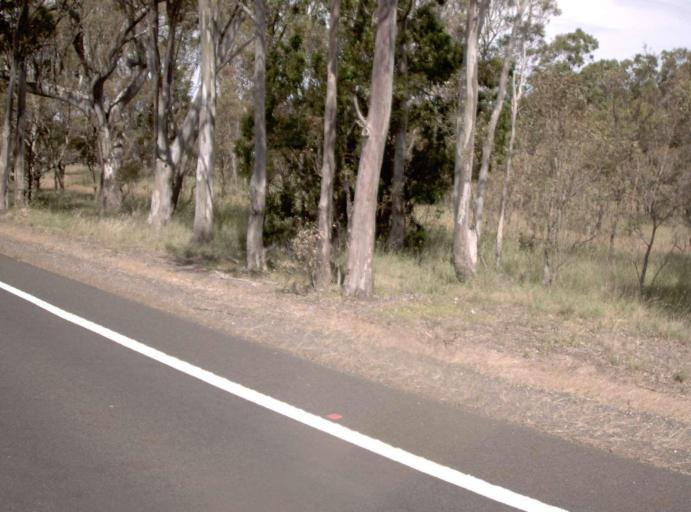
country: AU
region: Victoria
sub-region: East Gippsland
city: Bairnsdale
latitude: -37.8733
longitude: 147.4572
